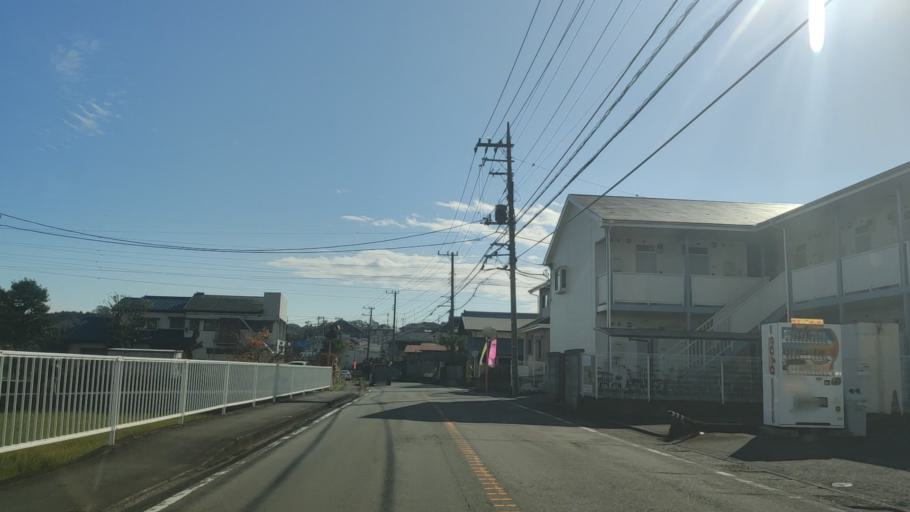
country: JP
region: Kanagawa
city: Atsugi
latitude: 35.4398
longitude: 139.3397
